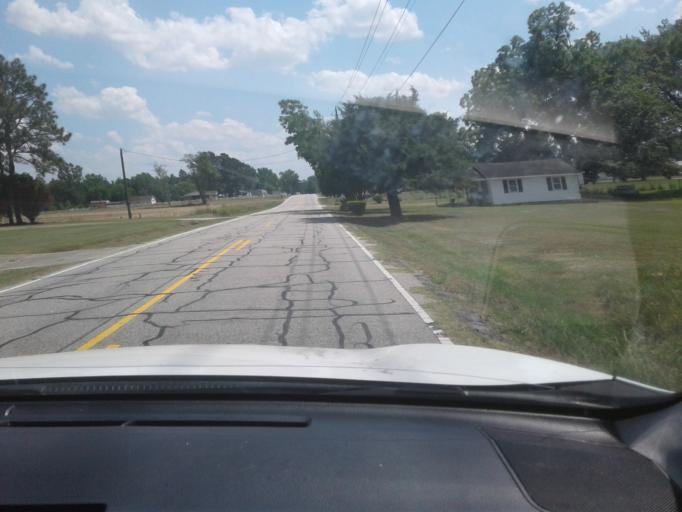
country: US
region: North Carolina
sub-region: Harnett County
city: Erwin
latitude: 35.2129
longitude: -78.6756
